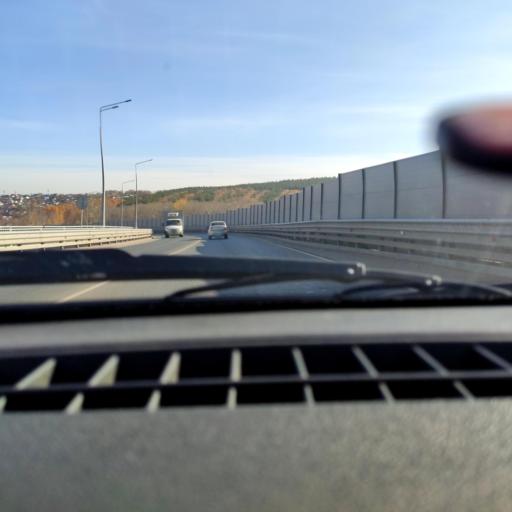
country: RU
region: Bashkortostan
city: Ufa
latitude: 54.8264
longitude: 56.1266
